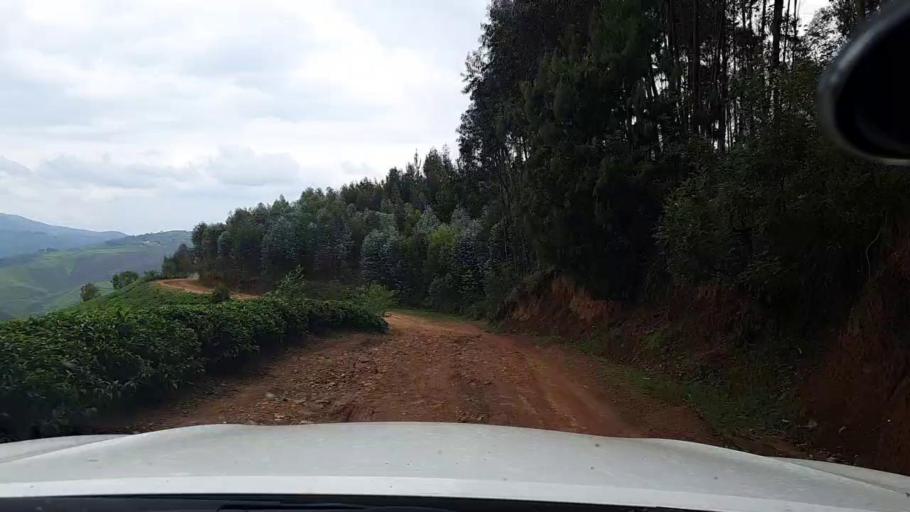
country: RW
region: Western Province
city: Kibuye
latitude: -2.1628
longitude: 29.4534
